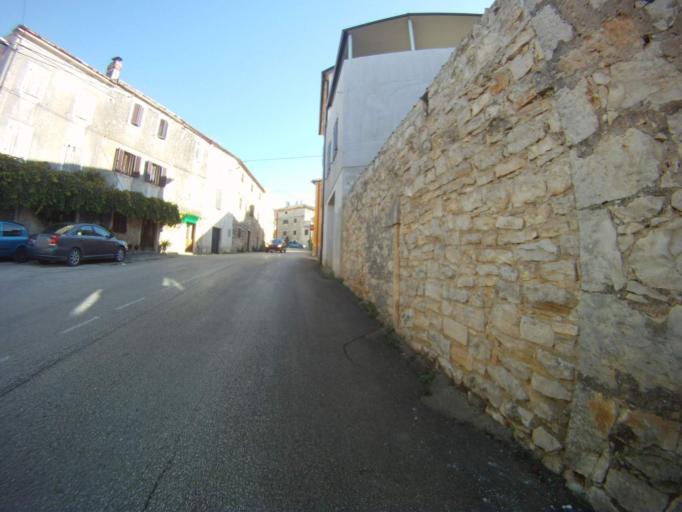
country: HR
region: Istarska
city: Buje
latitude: 45.3779
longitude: 13.6245
